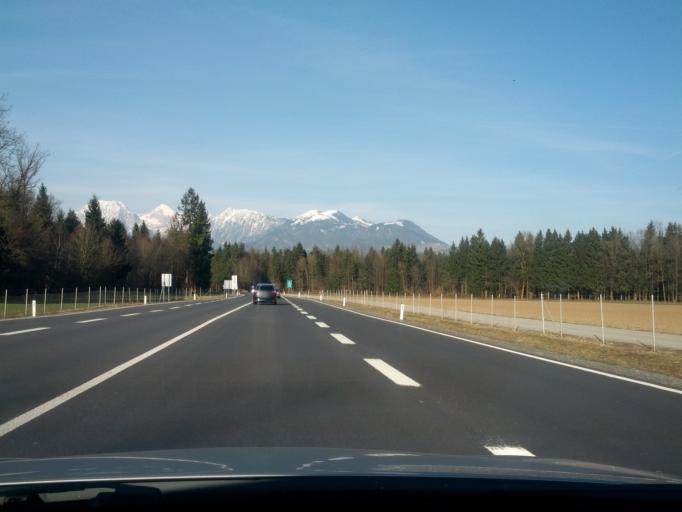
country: SI
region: Sencur
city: Sencur
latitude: 46.2210
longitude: 14.4395
